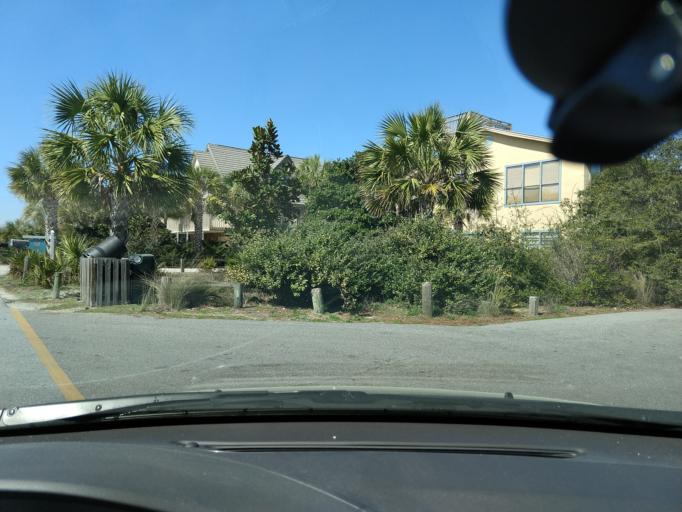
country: US
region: Florida
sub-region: Walton County
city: Seaside
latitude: 30.3363
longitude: -86.1922
